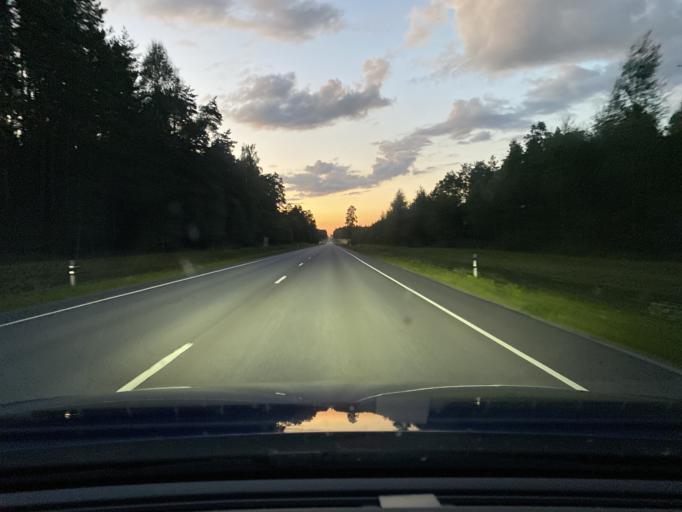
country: FI
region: Satakunta
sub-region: Pori
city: Vampula
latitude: 60.9363
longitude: 22.6830
